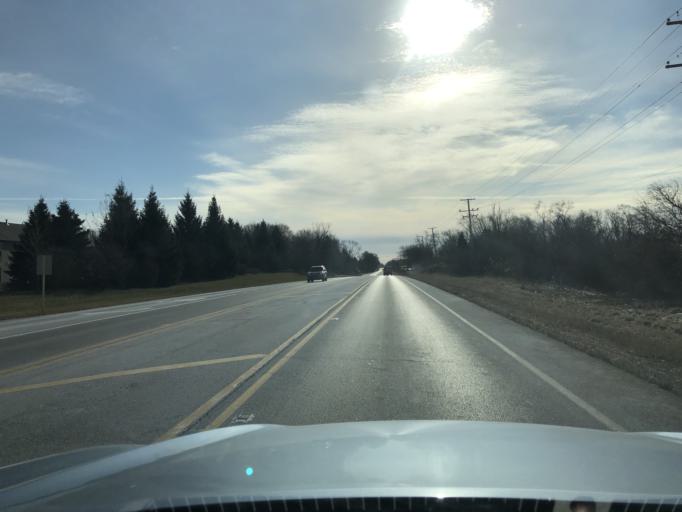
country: US
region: Illinois
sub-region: Lake County
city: Grandwood Park
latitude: 42.3945
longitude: -88.0041
